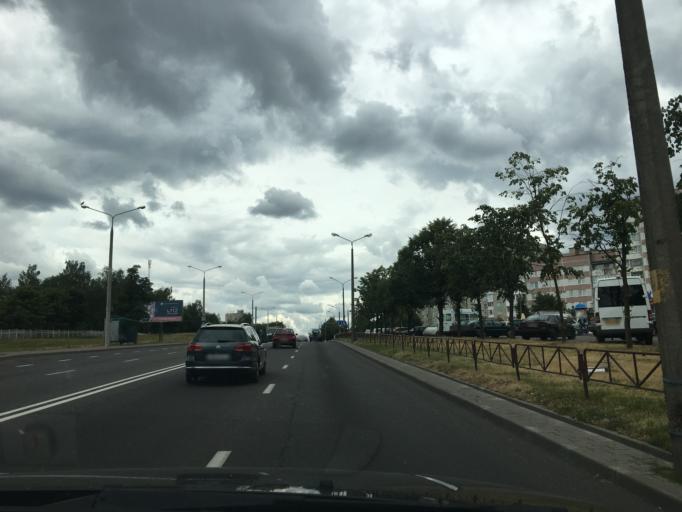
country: BY
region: Grodnenskaya
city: Hrodna
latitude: 53.6432
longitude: 23.8412
